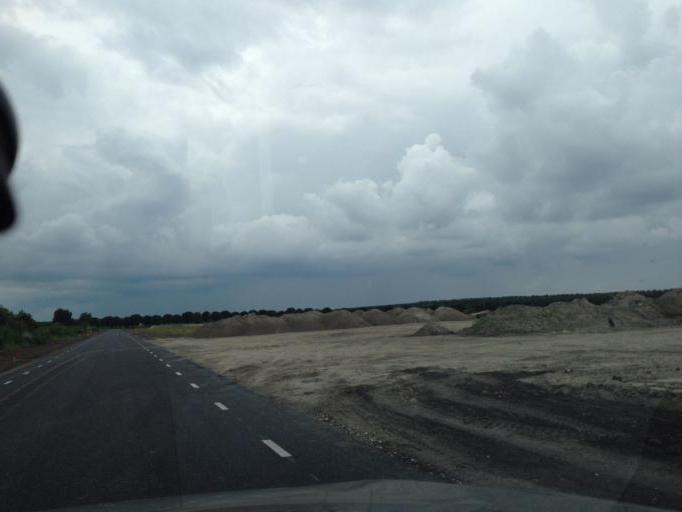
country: NL
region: Flevoland
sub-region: Gemeente Almere
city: Almere Stad
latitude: 52.3671
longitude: 5.2976
